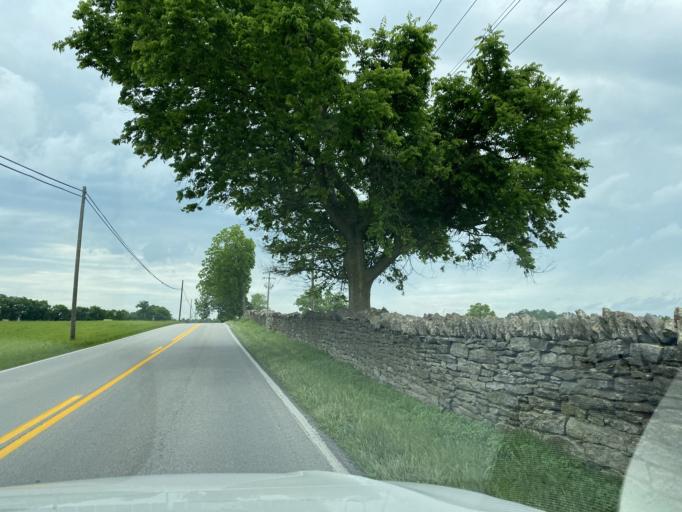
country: US
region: Kentucky
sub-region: Scott County
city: Georgetown
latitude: 38.2209
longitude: -84.5145
